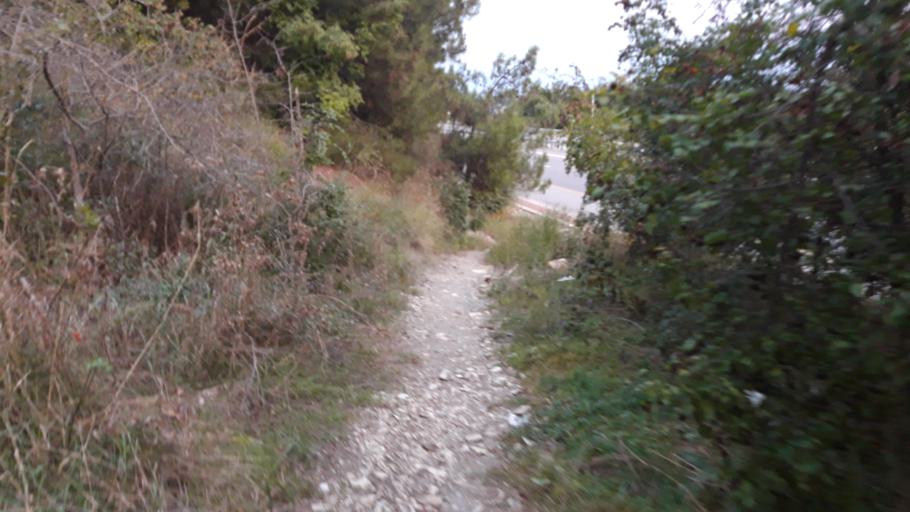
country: RU
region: Krasnodarskiy
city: Gelendzhik
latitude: 44.5794
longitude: 38.0858
